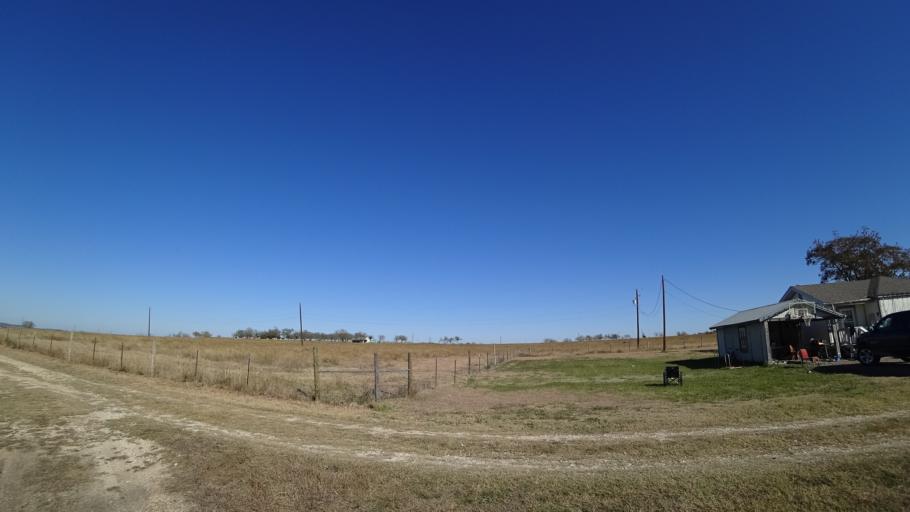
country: US
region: Texas
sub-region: Travis County
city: Garfield
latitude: 30.1182
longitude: -97.6484
